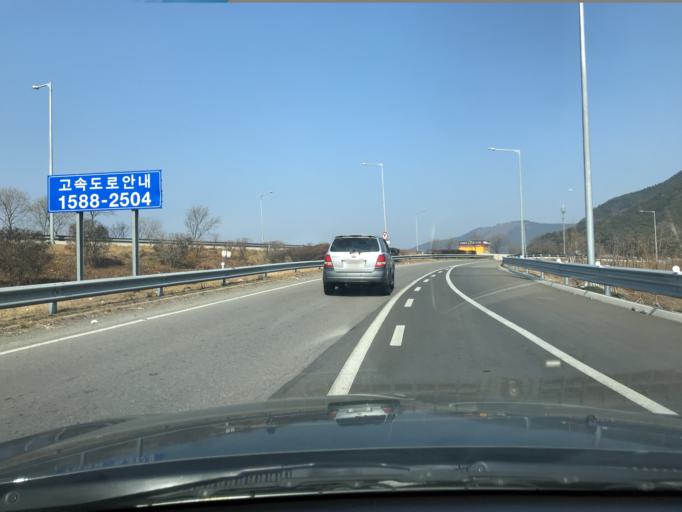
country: KR
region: Daegu
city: Hwawon
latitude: 35.7035
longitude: 128.4376
